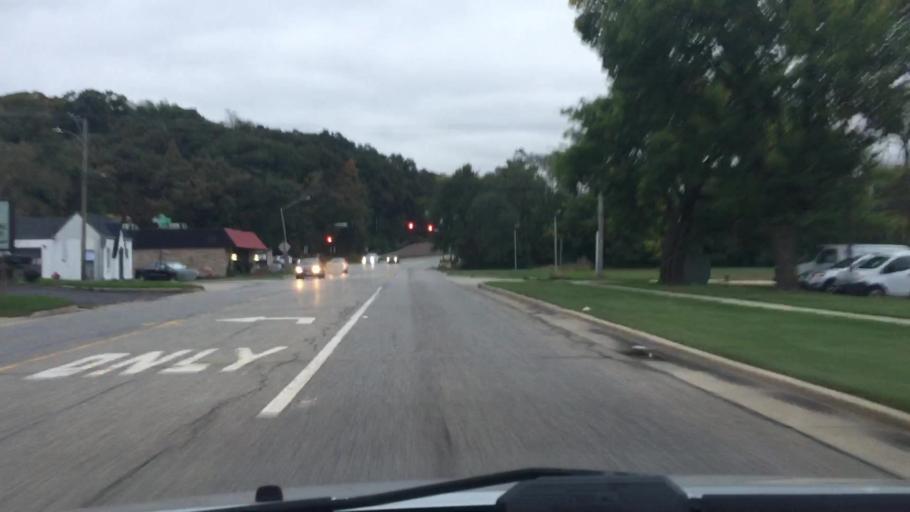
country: US
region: Illinois
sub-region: McHenry County
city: Algonquin
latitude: 42.1569
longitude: -88.2967
